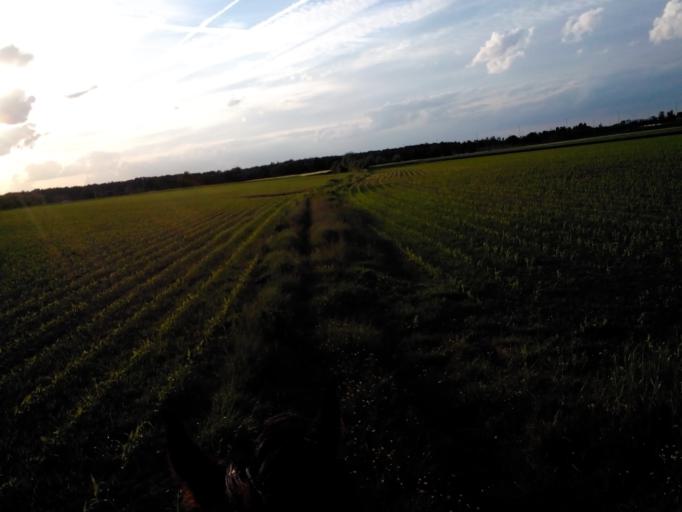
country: BE
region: Flanders
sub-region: Provincie Vlaams-Brabant
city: Bierbeek
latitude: 50.8385
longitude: 4.7192
